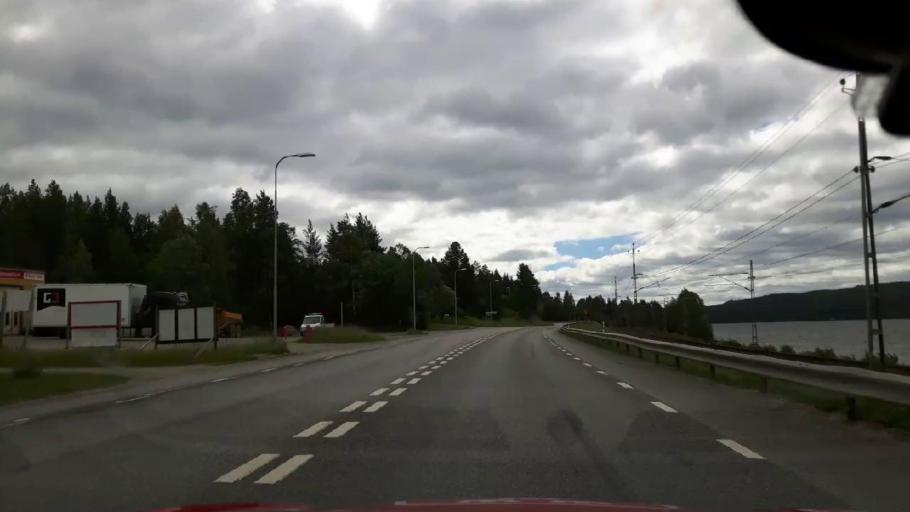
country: SE
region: Jaemtland
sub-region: Braecke Kommun
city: Braecke
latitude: 62.7429
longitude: 15.4265
